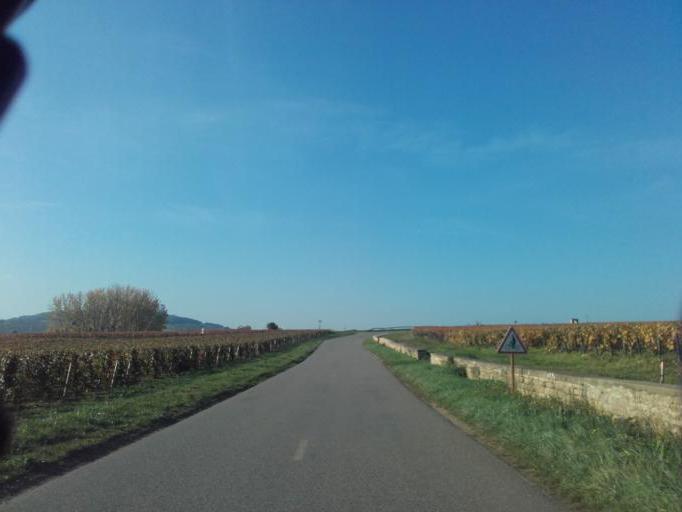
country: FR
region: Bourgogne
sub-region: Departement de Saone-et-Loire
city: Chagny
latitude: 46.9150
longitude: 4.7111
